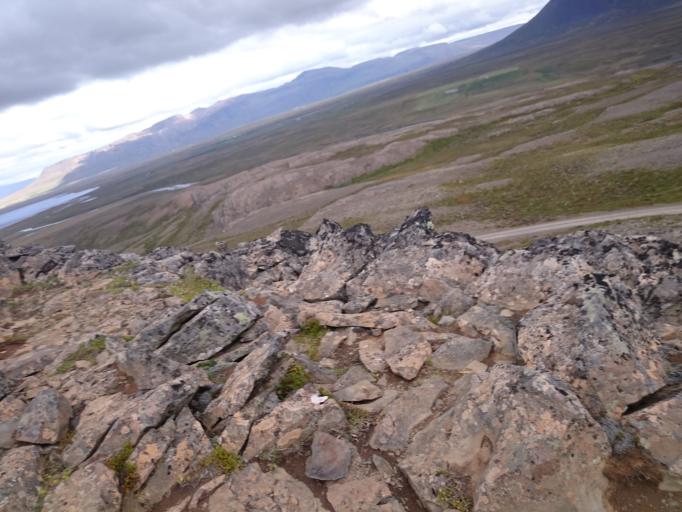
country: IS
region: Northwest
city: Saudarkrokur
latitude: 65.4748
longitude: -20.5966
